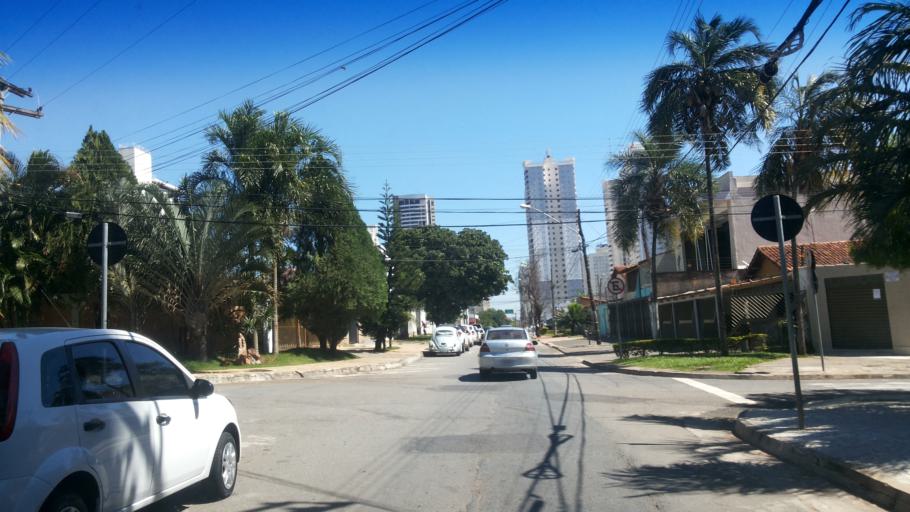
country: BR
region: Goias
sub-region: Goiania
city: Goiania
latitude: -16.7202
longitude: -49.2608
